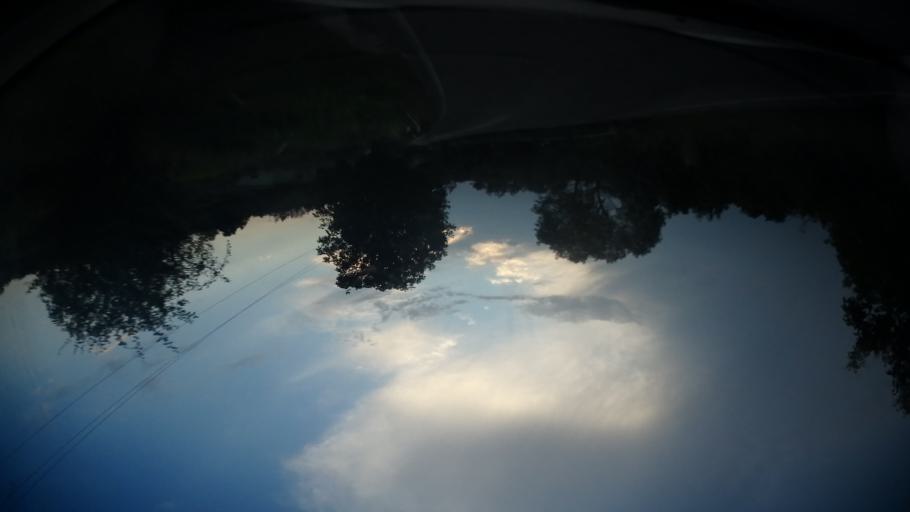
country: CZ
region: South Moravian
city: Dolni Kounice
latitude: 49.0704
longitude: 16.4787
